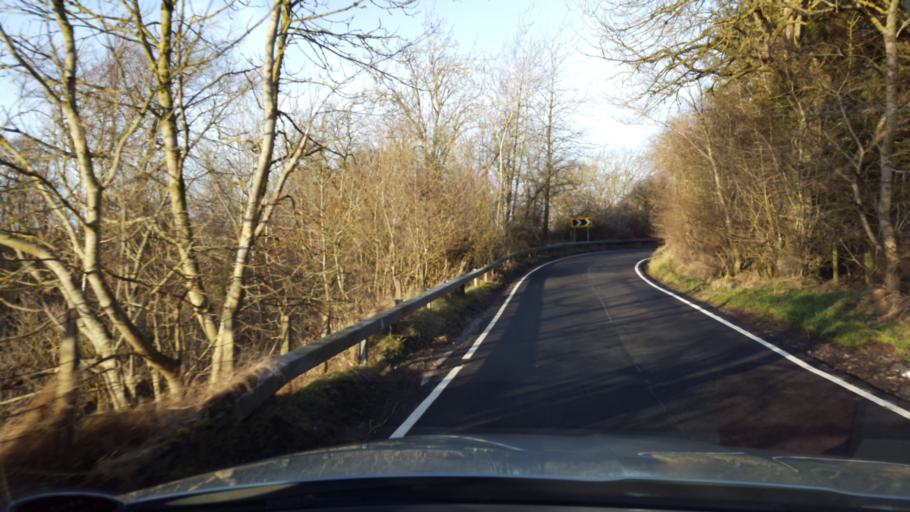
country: GB
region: Scotland
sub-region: West Lothian
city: Livingston
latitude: 55.8547
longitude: -3.5141
